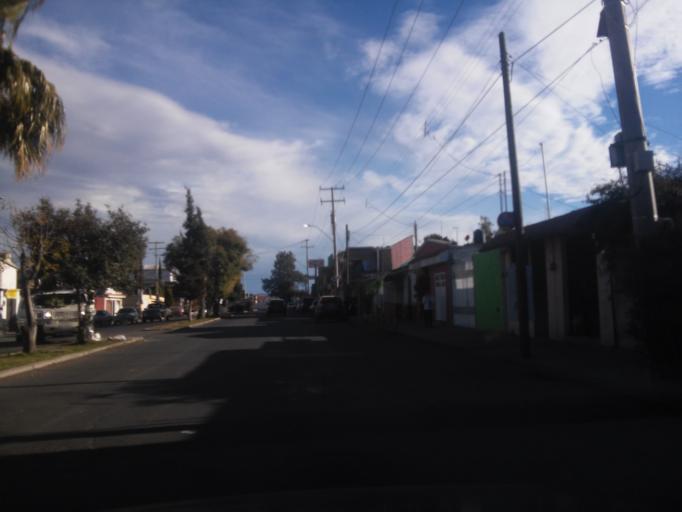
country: MX
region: Durango
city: Victoria de Durango
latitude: 24.0034
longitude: -104.6440
